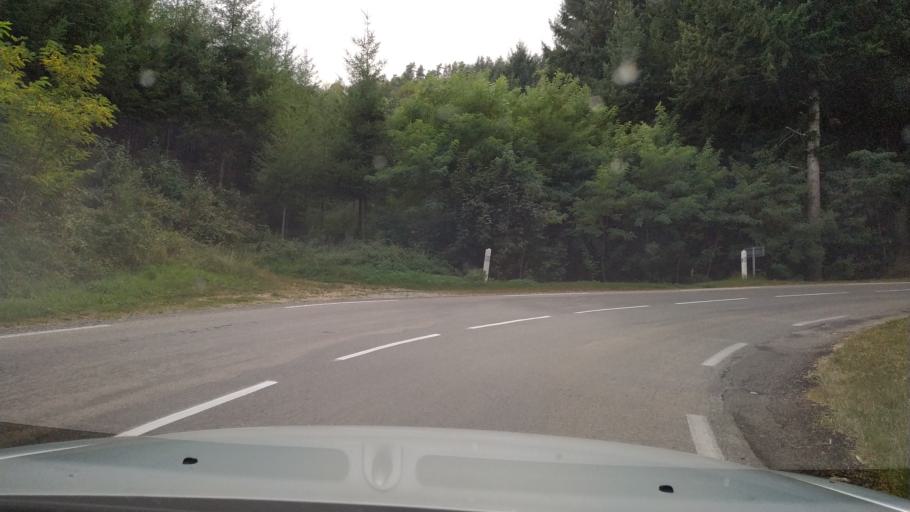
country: FR
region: Rhone-Alpes
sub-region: Departement de l'Ardeche
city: Desaignes
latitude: 44.9989
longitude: 4.5071
